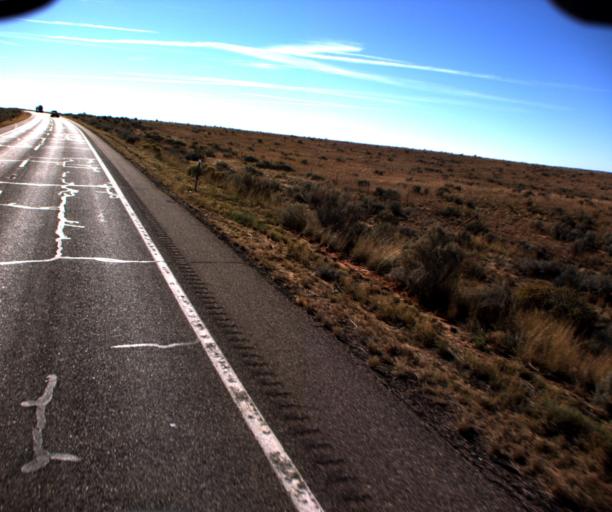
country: US
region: Arizona
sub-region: Mohave County
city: Colorado City
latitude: 36.8903
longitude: -112.9108
